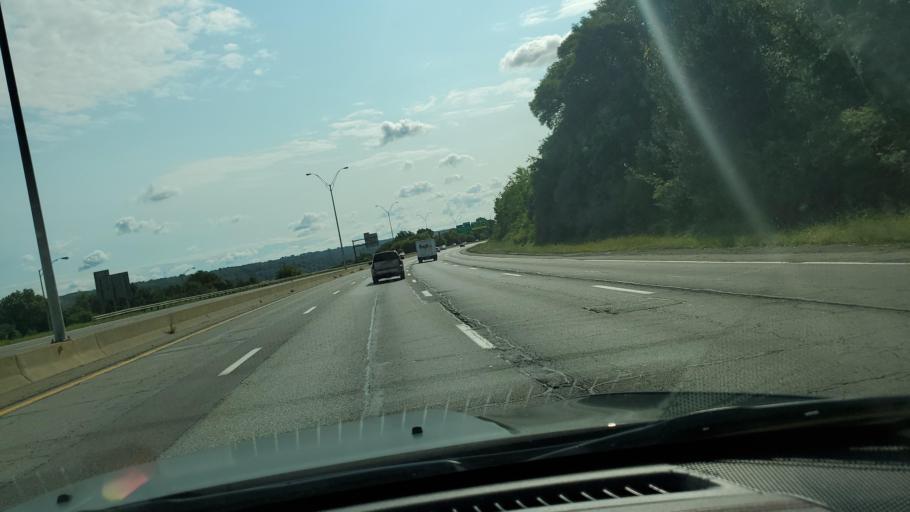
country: US
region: Ohio
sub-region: Mahoning County
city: Youngstown
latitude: 41.0814
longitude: -80.6393
